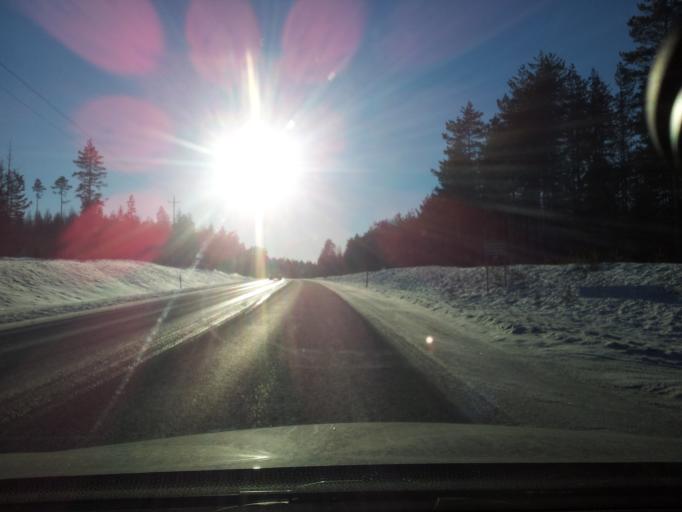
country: FI
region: Uusimaa
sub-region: Helsinki
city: Vihti
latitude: 60.3648
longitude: 24.3587
